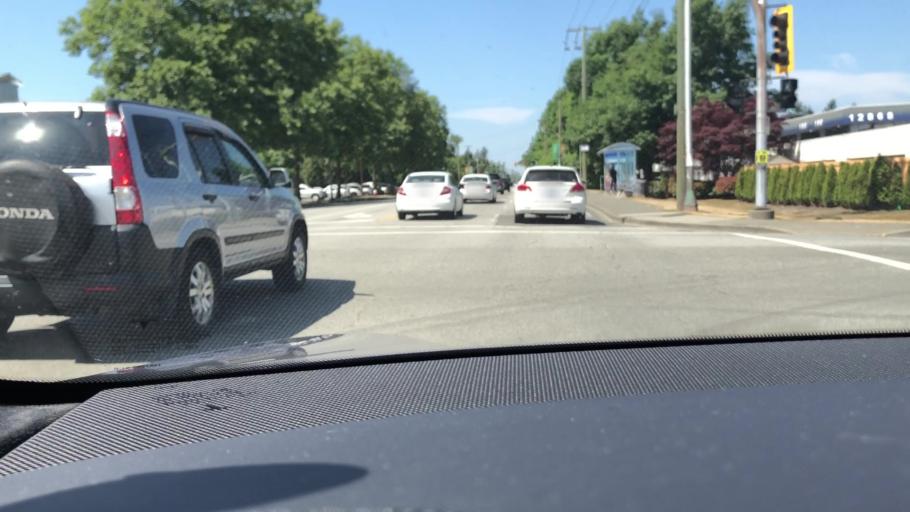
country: CA
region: British Columbia
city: Richmond
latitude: 49.1846
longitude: -123.0802
